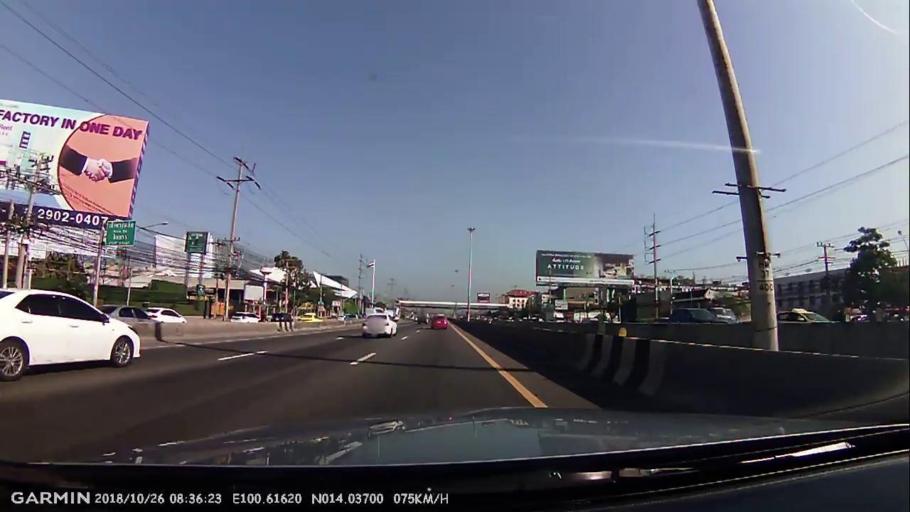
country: TH
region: Pathum Thani
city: Khlong Luang
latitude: 14.0373
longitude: 100.6162
